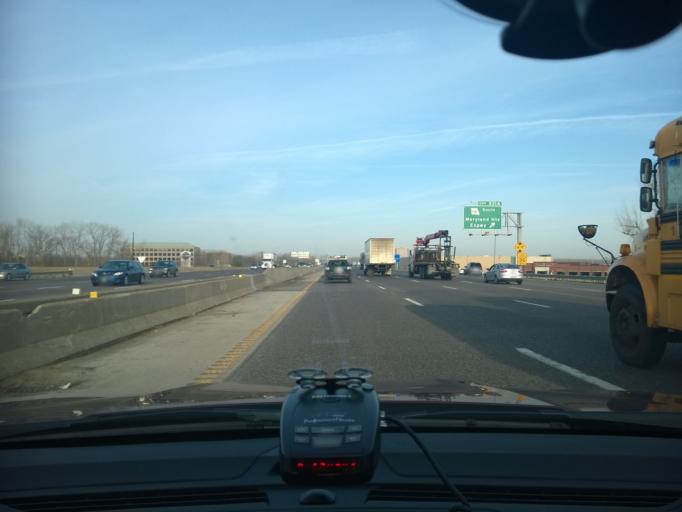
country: US
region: Missouri
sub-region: Saint Charles County
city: Saint Charles
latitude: 38.7558
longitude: -90.4590
